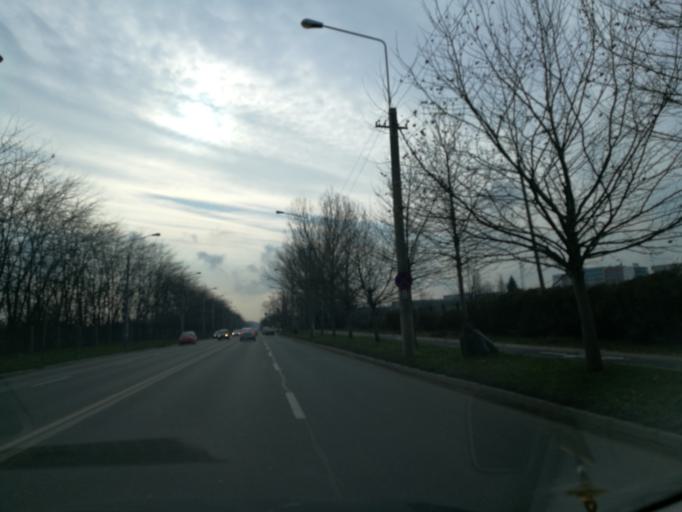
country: RO
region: Ilfov
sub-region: Comuna Fundeni-Dobroesti
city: Fundeni
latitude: 44.4843
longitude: 26.1259
